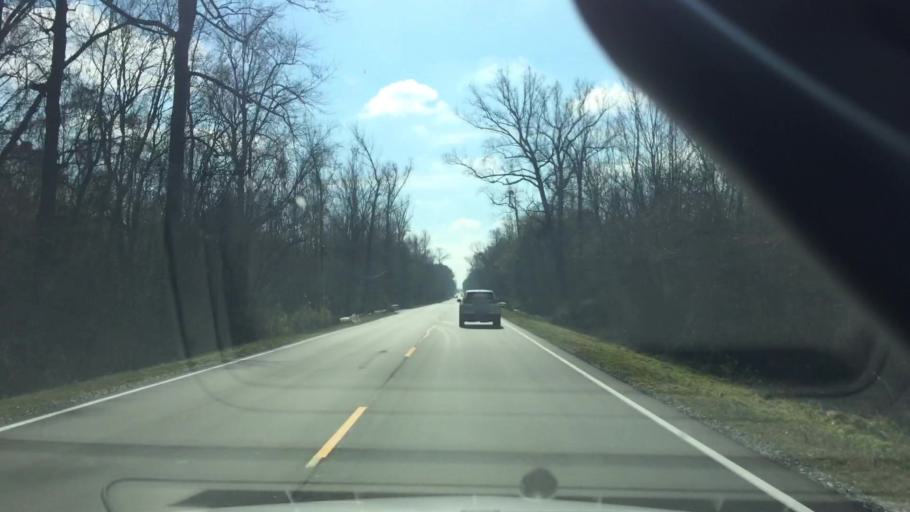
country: US
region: North Carolina
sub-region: Duplin County
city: Beulaville
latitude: 34.9468
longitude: -77.7680
